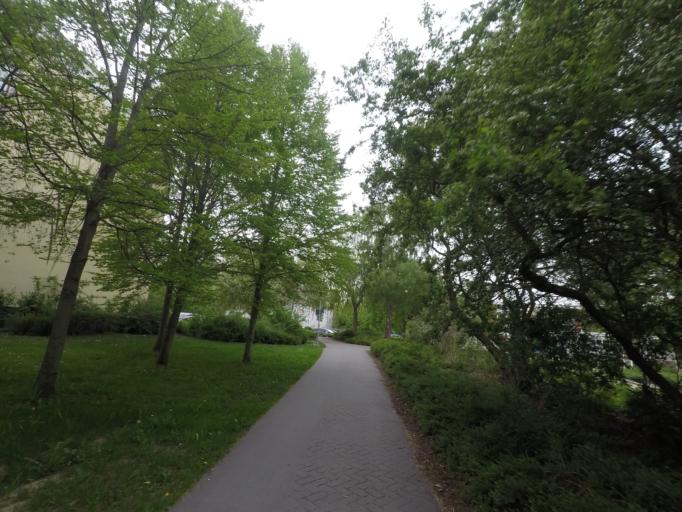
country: DE
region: Mecklenburg-Vorpommern
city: Rostock
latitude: 54.0685
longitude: 12.1229
